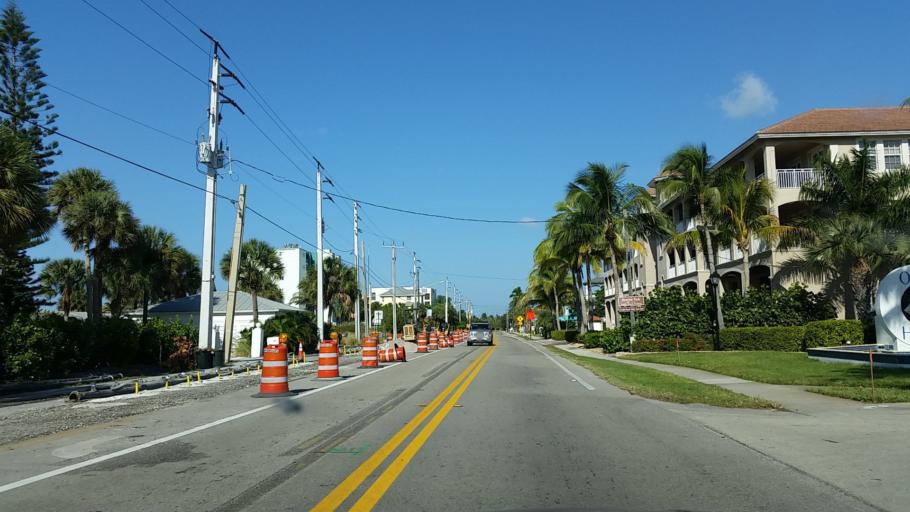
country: US
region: Florida
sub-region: Lee County
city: Fort Myers Beach
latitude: 26.4365
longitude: -81.9209
